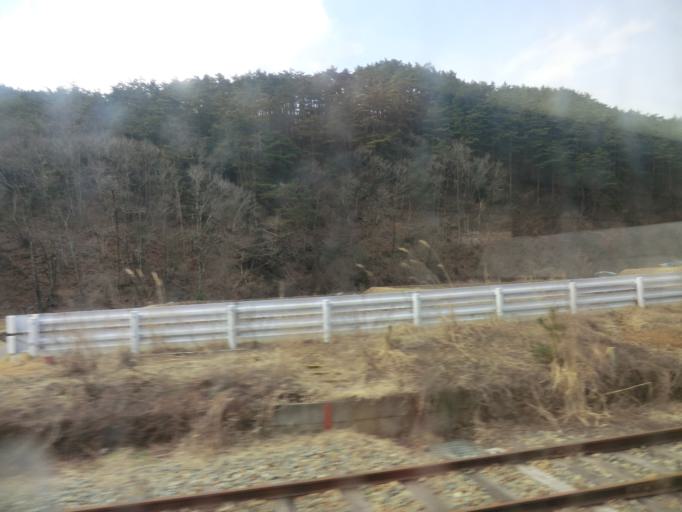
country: JP
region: Nagano
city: Ueda
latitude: 36.4580
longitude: 138.0795
